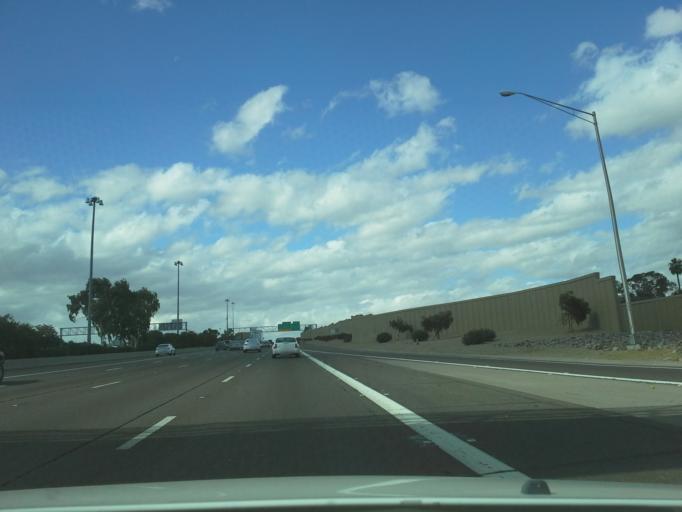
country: US
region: Arizona
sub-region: Maricopa County
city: Phoenix
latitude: 33.4615
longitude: -112.0870
